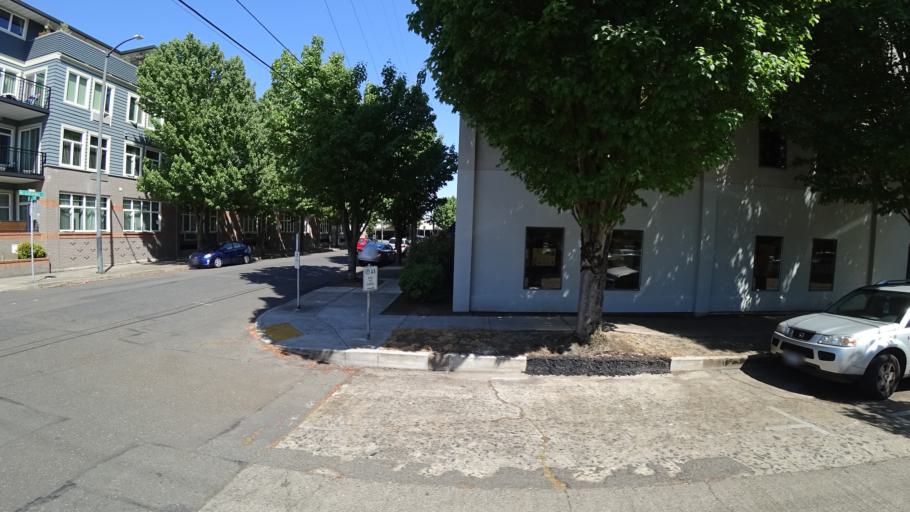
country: US
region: Oregon
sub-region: Multnomah County
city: Portland
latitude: 45.5328
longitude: -122.6596
